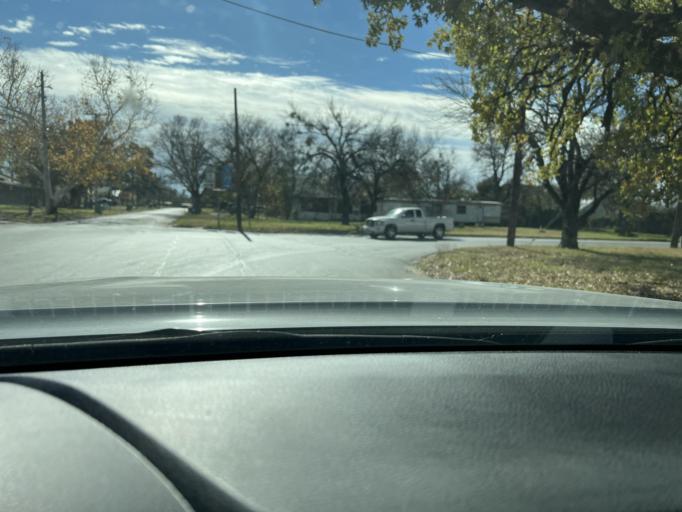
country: US
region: Texas
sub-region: Eastland County
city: Eastland
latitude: 32.3894
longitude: -98.8181
